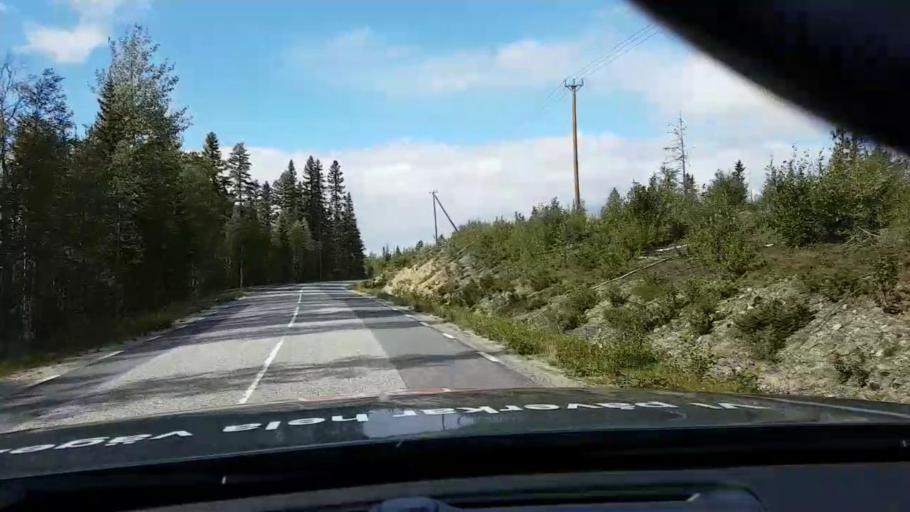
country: SE
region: Vaesterbotten
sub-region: Asele Kommun
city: Asele
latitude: 63.8262
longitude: 17.4746
